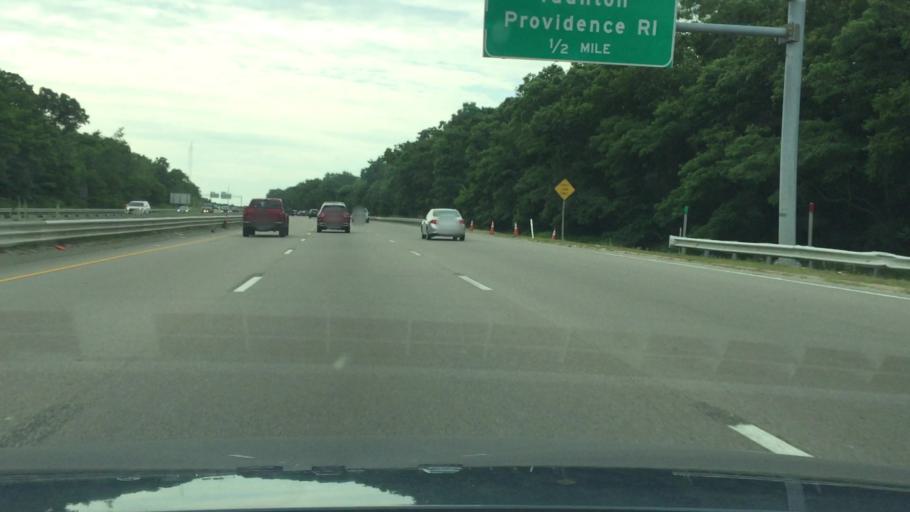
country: US
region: Massachusetts
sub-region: Plymouth County
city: North Plymouth
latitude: 41.9583
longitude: -70.6861
